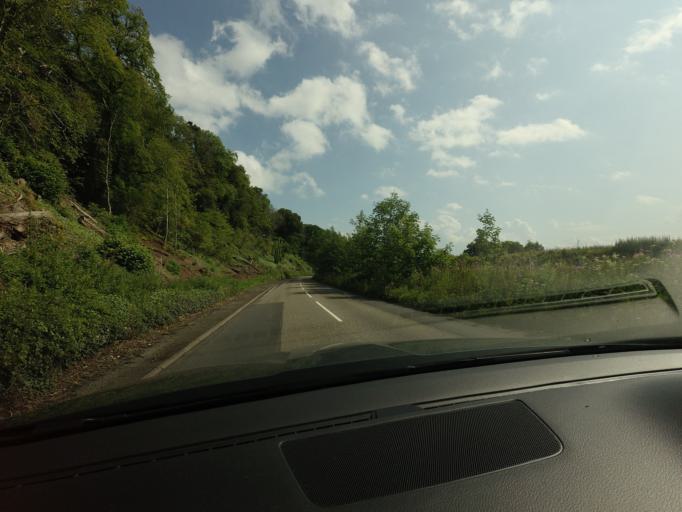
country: GB
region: Scotland
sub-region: Highland
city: Dingwall
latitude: 57.6084
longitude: -4.4131
